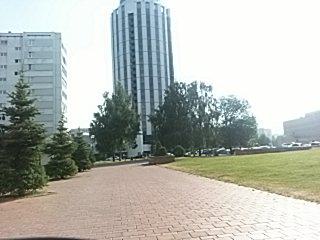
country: RU
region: Tatarstan
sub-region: Tukayevskiy Rayon
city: Naberezhnyye Chelny
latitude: 55.7417
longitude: 52.4157
